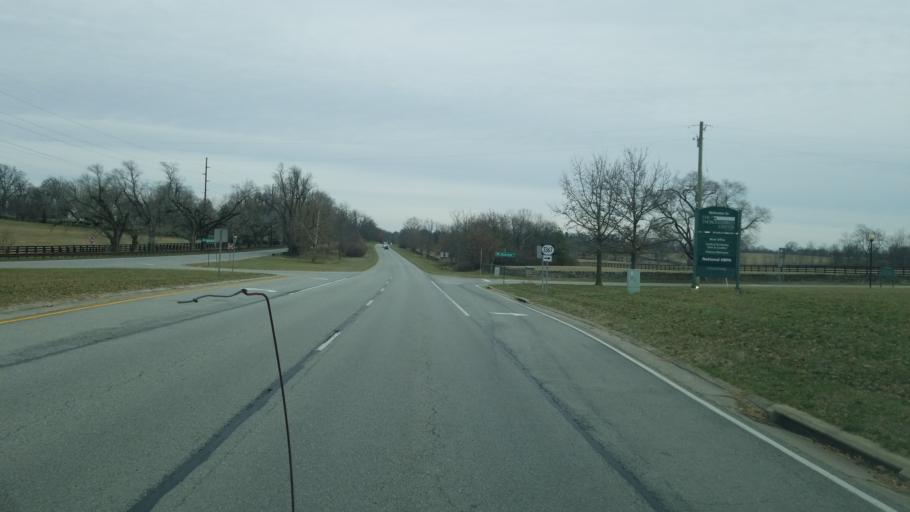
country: US
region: Kentucky
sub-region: Fayette County
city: Lexington-Fayette
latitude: 38.0979
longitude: -84.4209
